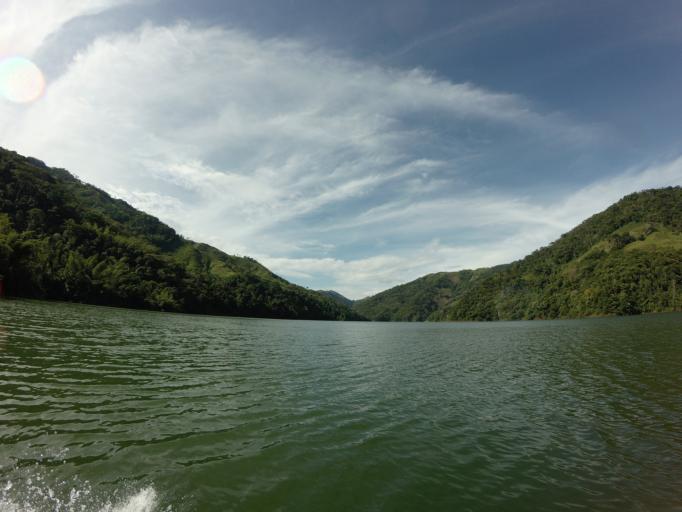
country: CO
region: Caldas
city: Norcasia
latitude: 5.5376
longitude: -74.9186
